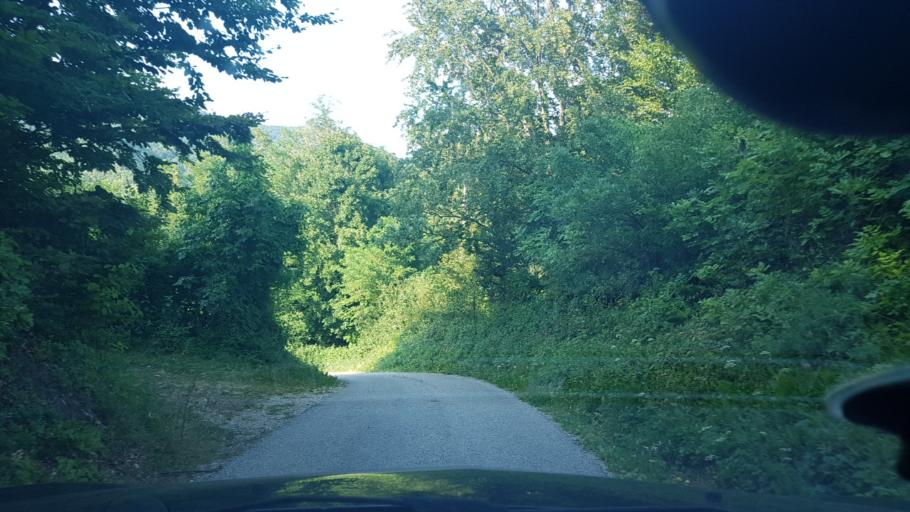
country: HR
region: Krapinsko-Zagorska
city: Radoboj
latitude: 46.1721
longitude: 15.9022
